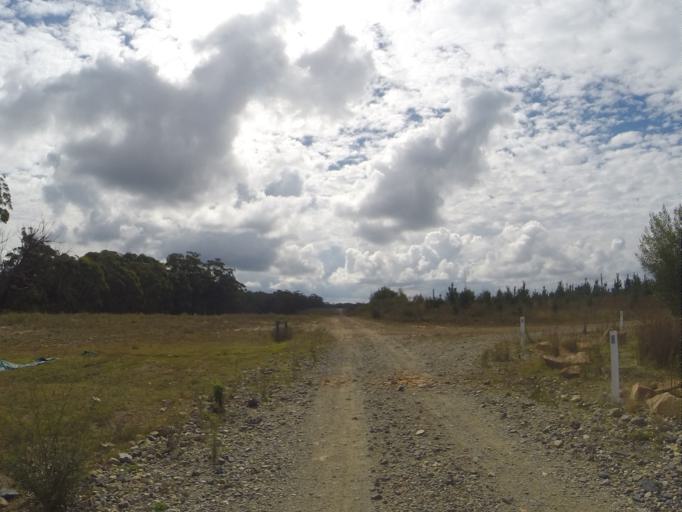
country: AU
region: New South Wales
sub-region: Wingecarribee
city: Moss Vale
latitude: -34.5123
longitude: 150.2273
